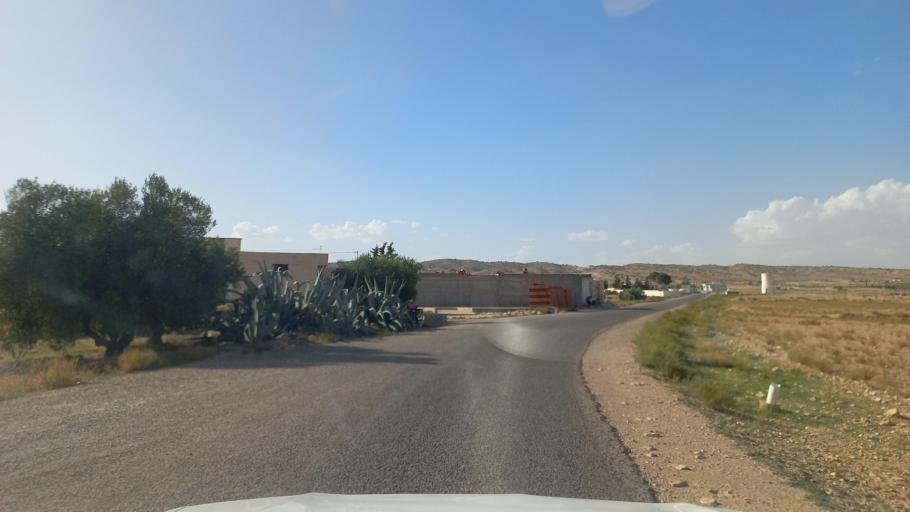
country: TN
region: Al Qasrayn
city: Sbiba
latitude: 35.3413
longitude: 8.9919
